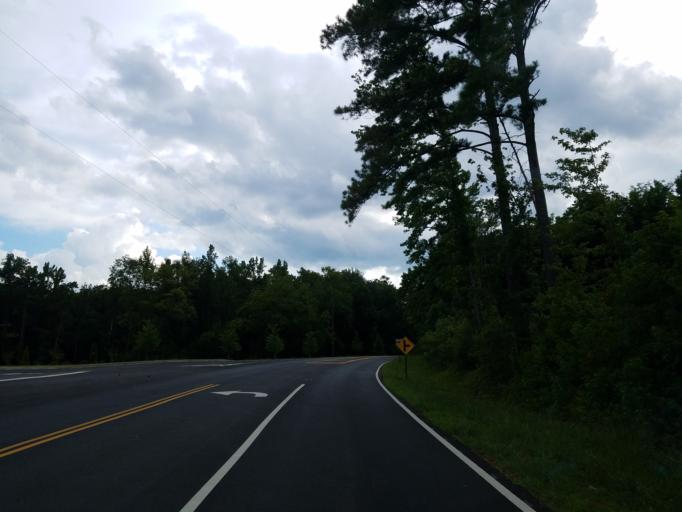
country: US
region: Georgia
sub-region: Bartow County
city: Cartersville
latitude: 34.2673
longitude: -84.8301
